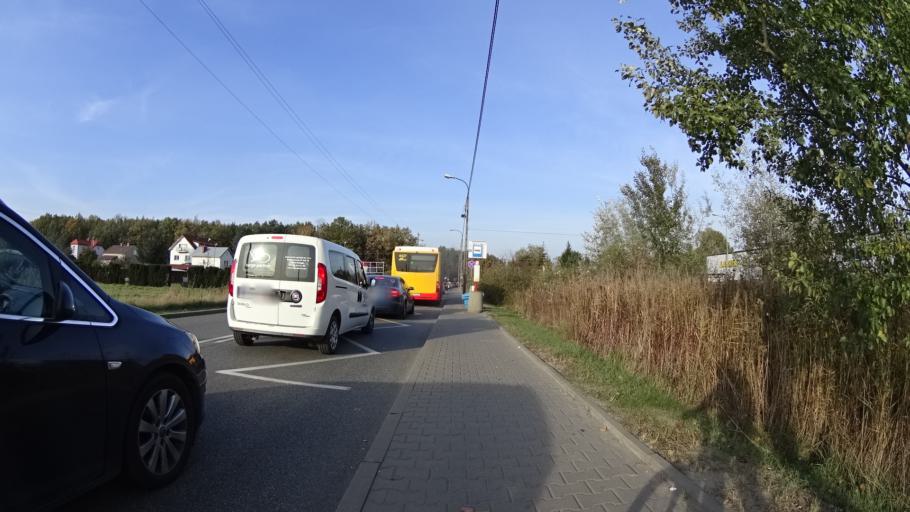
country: PL
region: Masovian Voivodeship
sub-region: Powiat warszawski zachodni
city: Lomianki
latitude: 52.2927
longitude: 20.8772
